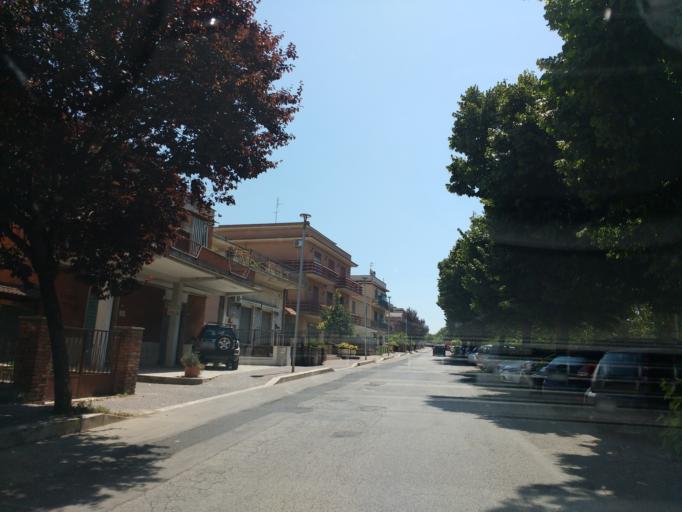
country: IT
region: Latium
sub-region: Citta metropolitana di Roma Capitale
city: Villa Adriana
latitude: 41.9500
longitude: 12.7712
